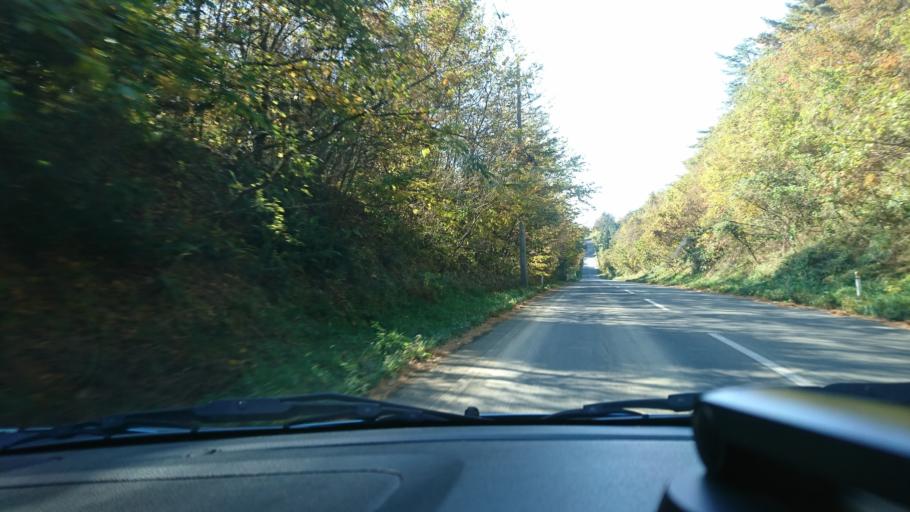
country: JP
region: Iwate
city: Ichinoseki
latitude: 38.8139
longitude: 141.2652
